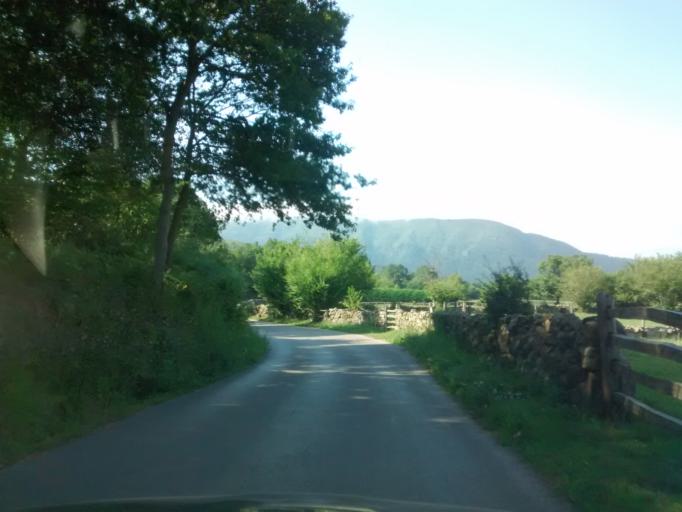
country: ES
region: Cantabria
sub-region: Provincia de Cantabria
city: Ruente
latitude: 43.2483
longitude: -4.2418
